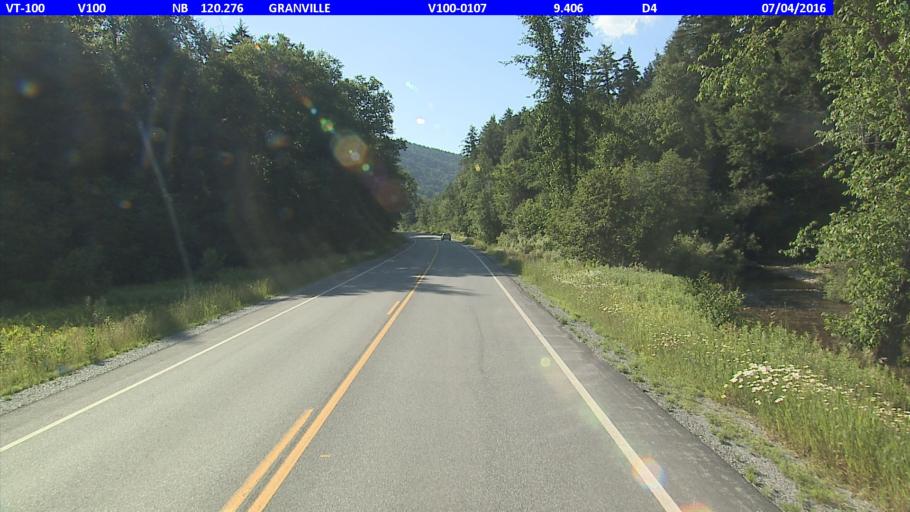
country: US
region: Vermont
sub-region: Washington County
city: Northfield
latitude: 44.0590
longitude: -72.8473
